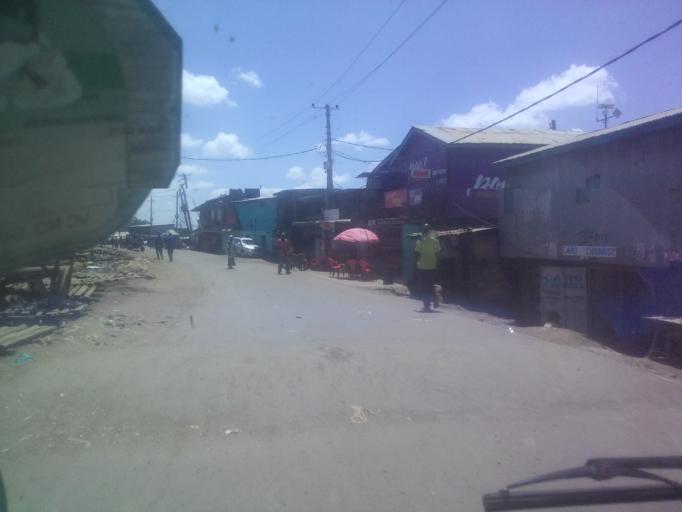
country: KE
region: Nairobi Area
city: Nairobi
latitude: -1.3152
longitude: 36.7968
